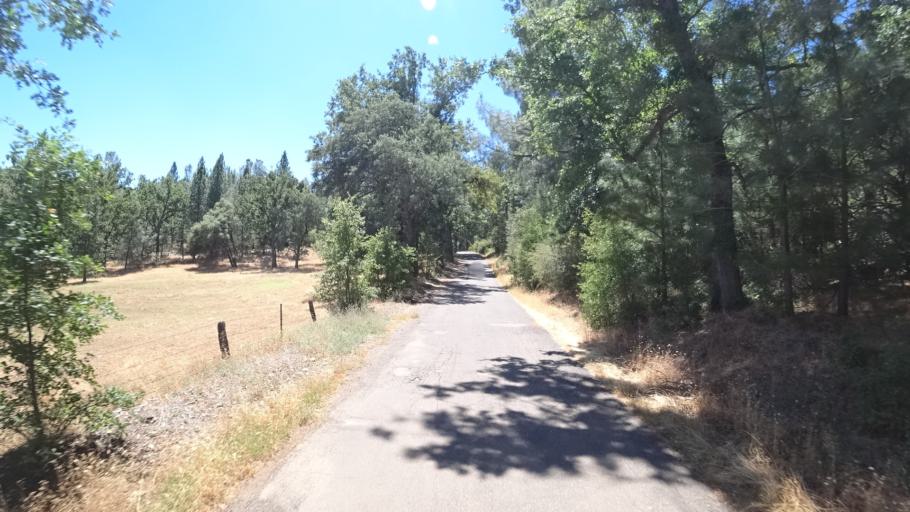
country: US
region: California
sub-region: Calaveras County
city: Forest Meadows
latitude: 38.2429
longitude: -120.4380
